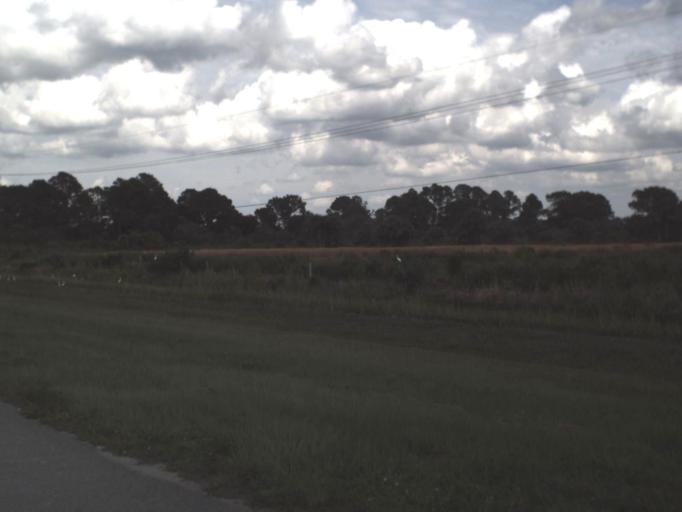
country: US
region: Florida
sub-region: Hendry County
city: Port LaBelle
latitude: 26.6395
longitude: -81.4363
